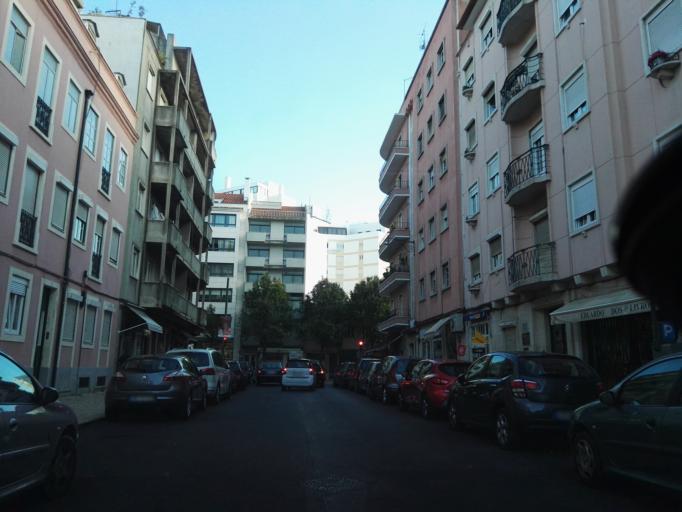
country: PT
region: Lisbon
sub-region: Lisbon
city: Lisbon
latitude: 38.7158
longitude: -9.1653
